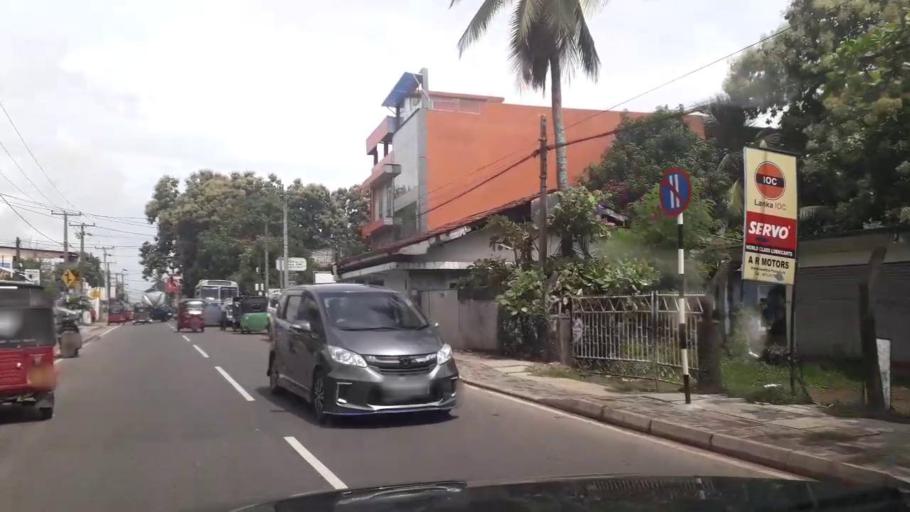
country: LK
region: Western
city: Moratuwa
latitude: 6.7508
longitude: 79.9002
